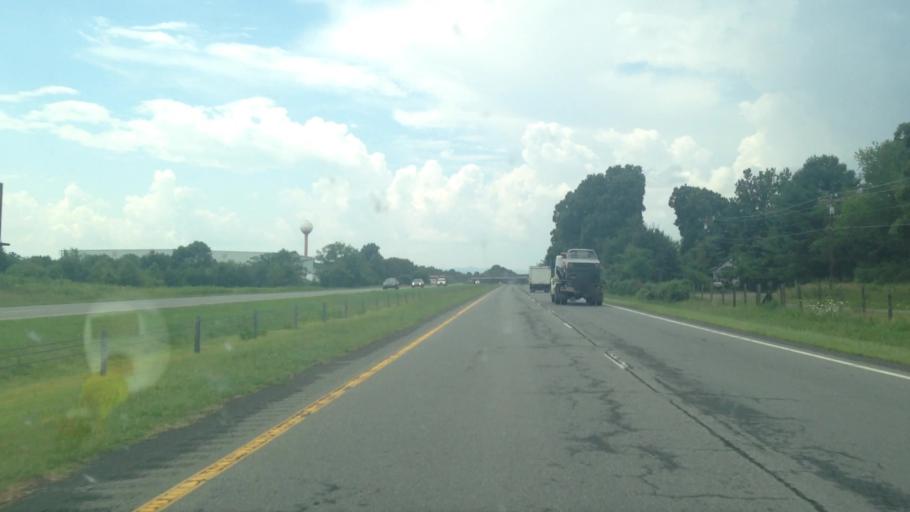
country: US
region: North Carolina
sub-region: Surry County
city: Flat Rock
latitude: 36.4560
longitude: -80.5566
